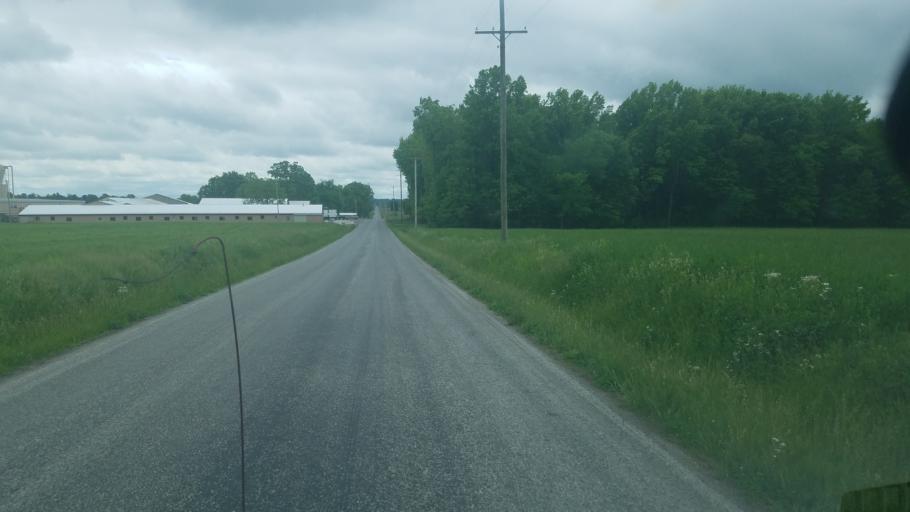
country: US
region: Ohio
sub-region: Wayne County
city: Dalton
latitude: 40.7690
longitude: -81.7551
